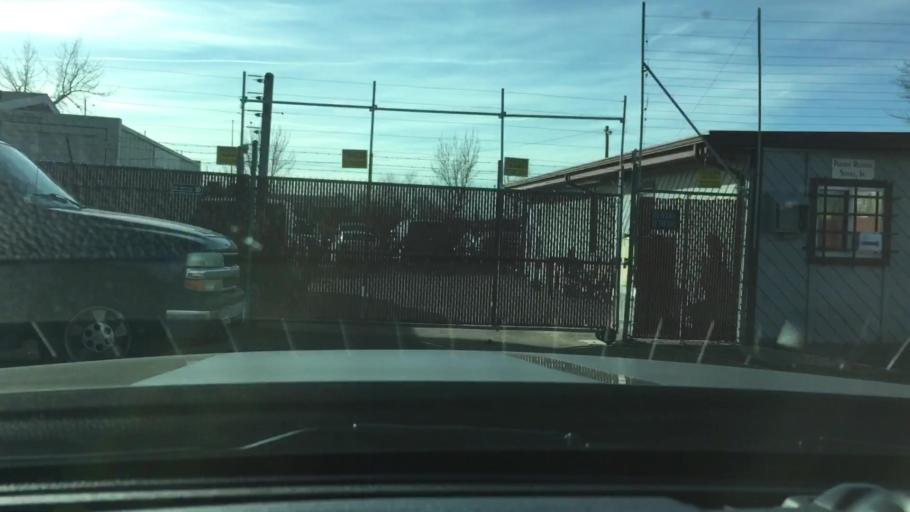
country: US
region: Colorado
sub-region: Adams County
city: Twin Lakes
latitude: 39.8271
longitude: -105.0051
